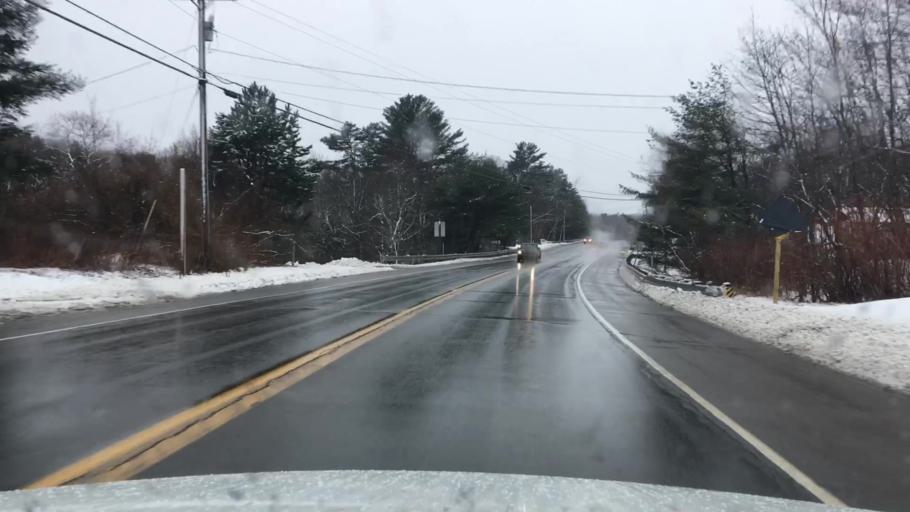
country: US
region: Maine
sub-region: Knox County
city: Rockport
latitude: 44.1802
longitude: -69.1390
